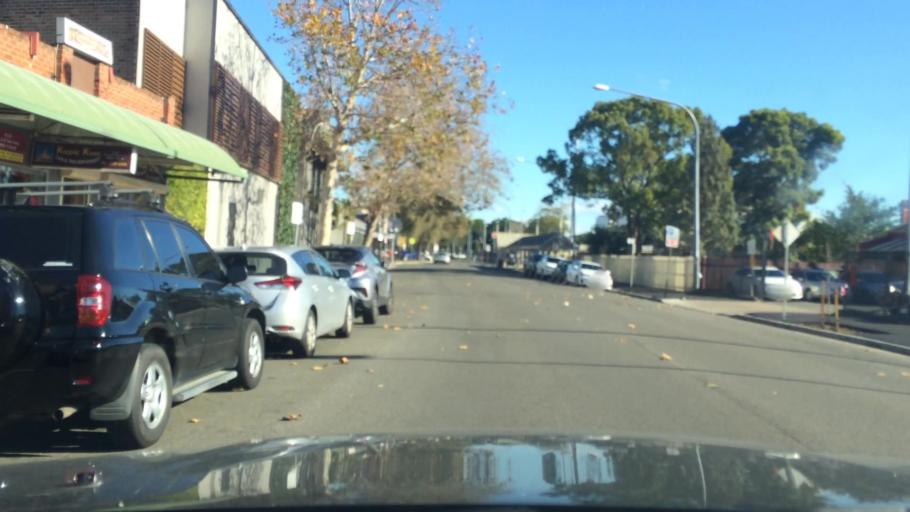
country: AU
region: New South Wales
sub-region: Fairfield
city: Carramar
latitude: -33.8722
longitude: 150.9581
